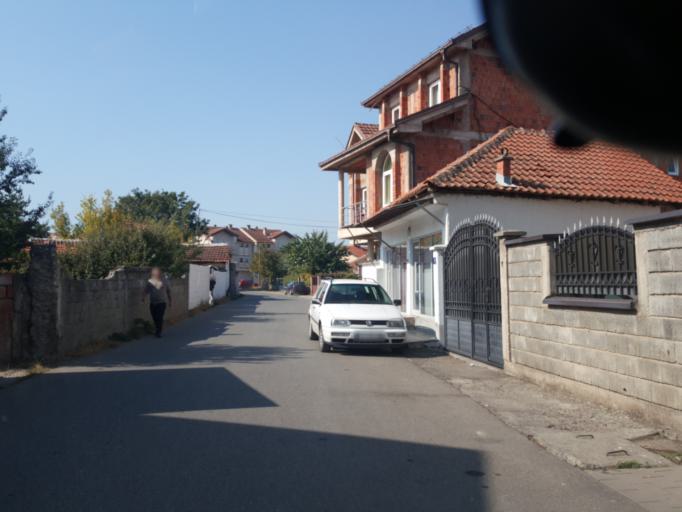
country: XK
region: Gjakova
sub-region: Komuna e Gjakoves
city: Gjakove
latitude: 42.3904
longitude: 20.4313
